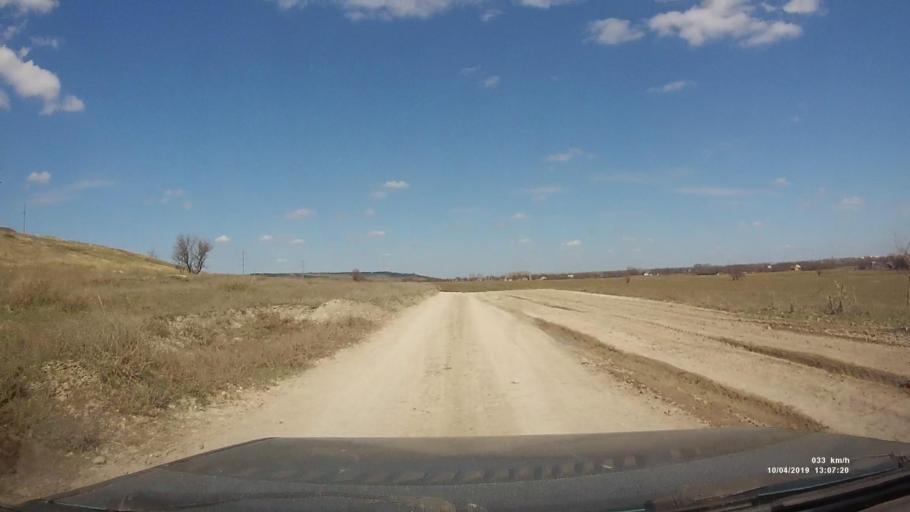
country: RU
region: Rostov
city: Masalovka
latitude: 48.3955
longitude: 40.2401
